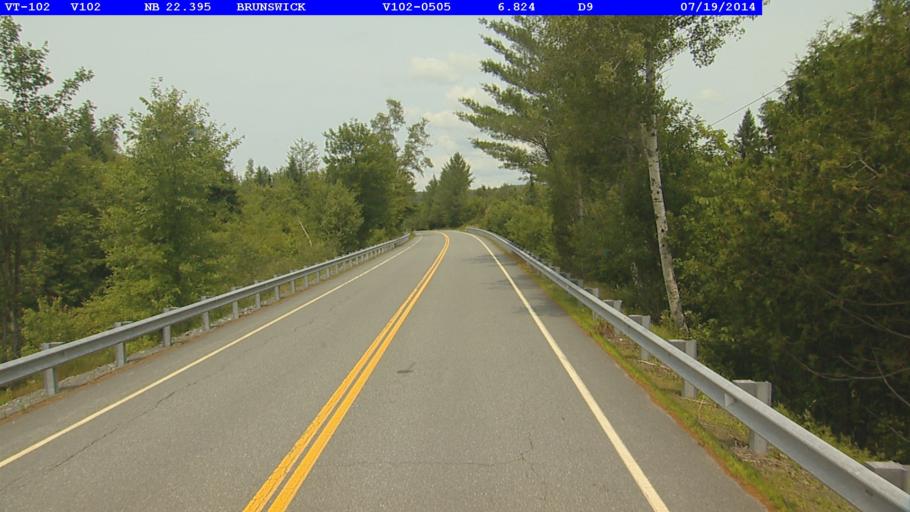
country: US
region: New Hampshire
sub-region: Coos County
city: Stratford
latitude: 44.7456
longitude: -71.6314
